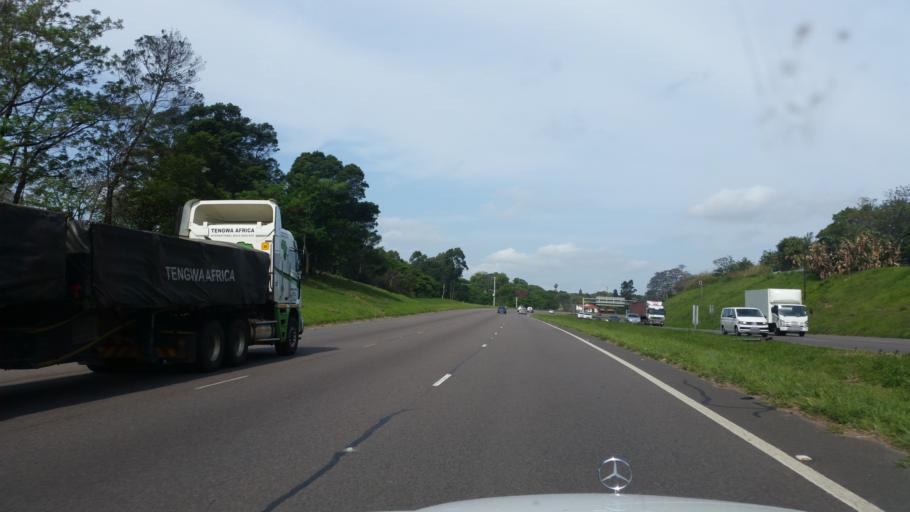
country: ZA
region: KwaZulu-Natal
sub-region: eThekwini Metropolitan Municipality
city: Berea
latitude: -29.8299
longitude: 30.8403
